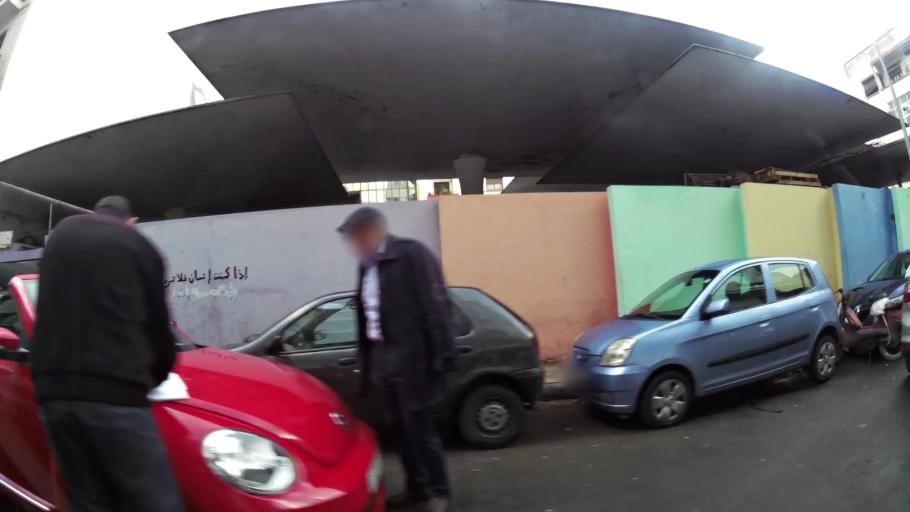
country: MA
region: Grand Casablanca
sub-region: Casablanca
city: Casablanca
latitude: 33.5862
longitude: -7.6208
